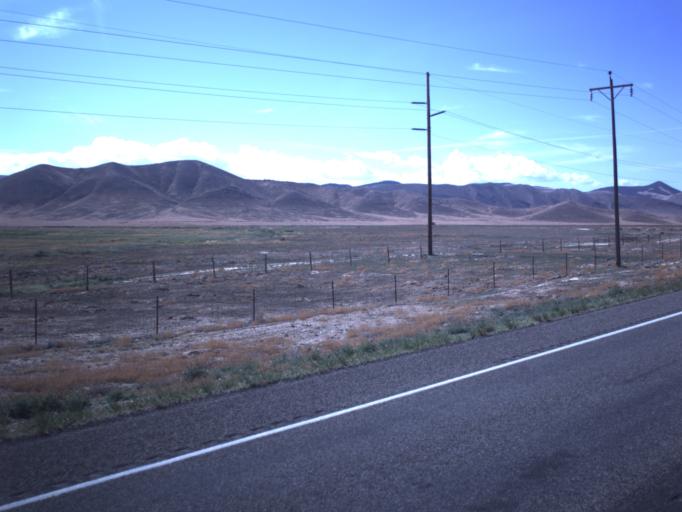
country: US
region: Utah
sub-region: Sevier County
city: Salina
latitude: 39.0351
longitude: -111.8284
